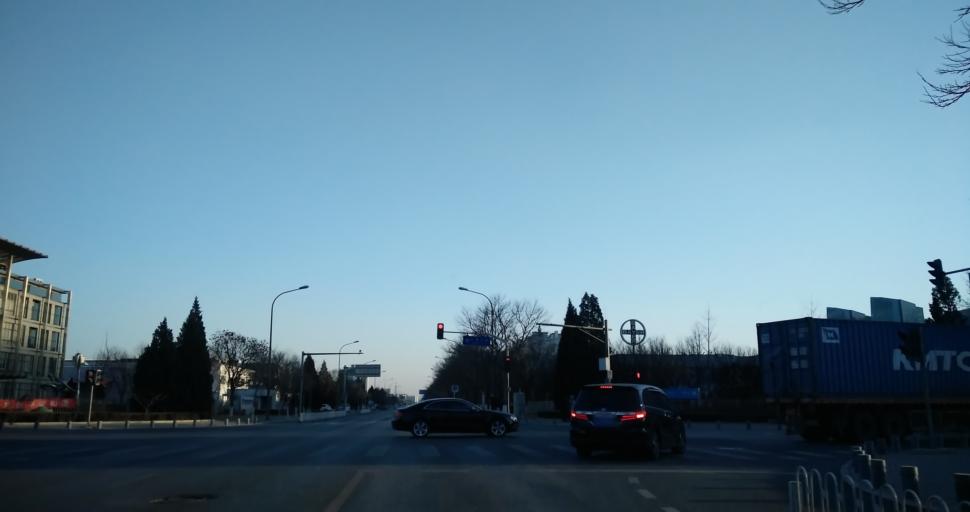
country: CN
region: Beijing
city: Jiugong
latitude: 39.7984
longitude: 116.5080
